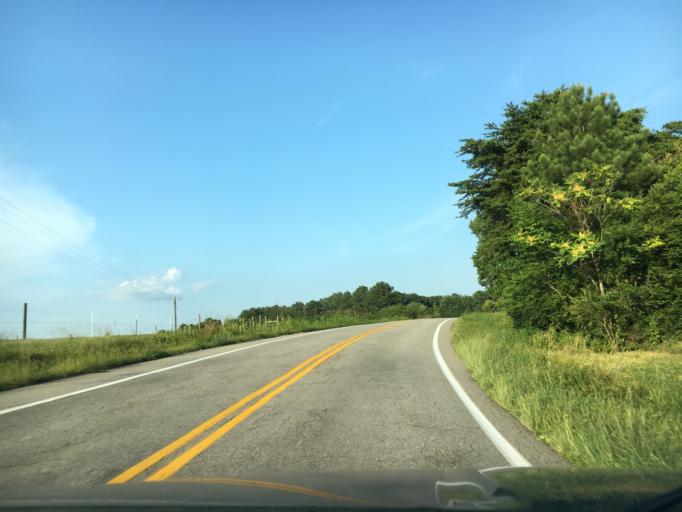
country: US
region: Virginia
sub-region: Pittsylvania County
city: Chatham
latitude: 36.8297
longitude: -79.2430
